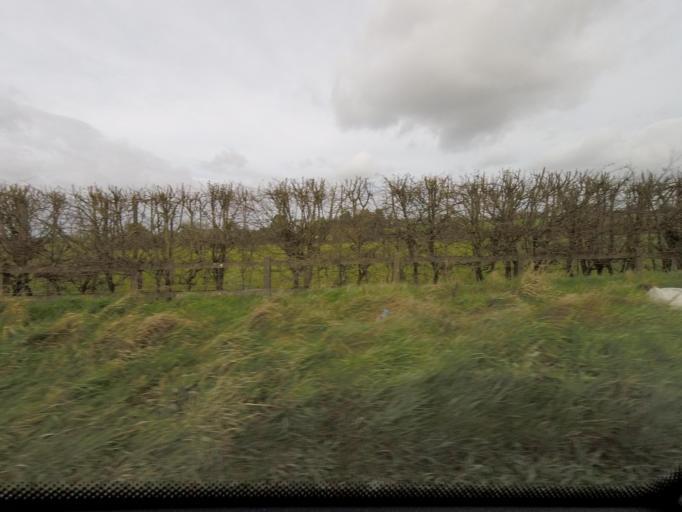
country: IE
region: Leinster
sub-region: Kildare
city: Johnstown
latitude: 53.2053
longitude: -6.6286
